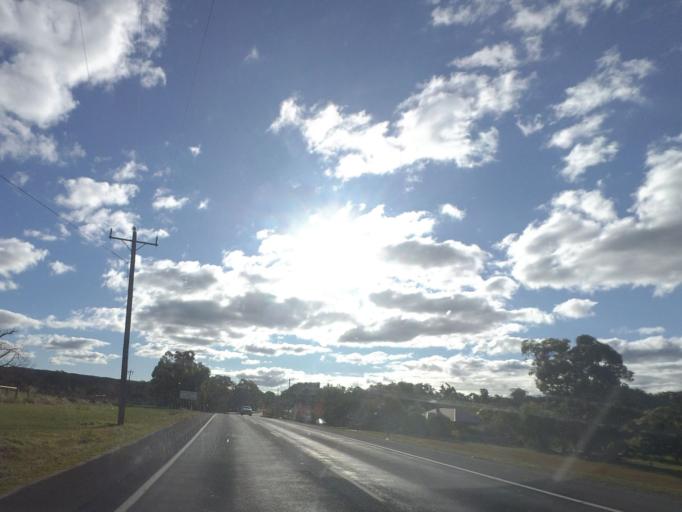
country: AU
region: Victoria
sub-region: Mount Alexander
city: Castlemaine
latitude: -37.1353
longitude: 144.3456
